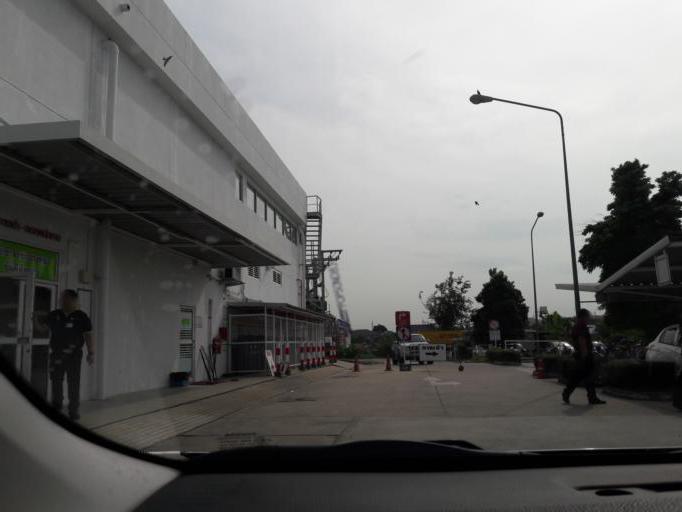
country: TH
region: Ang Thong
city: Ang Thong
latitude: 14.5804
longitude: 100.4583
